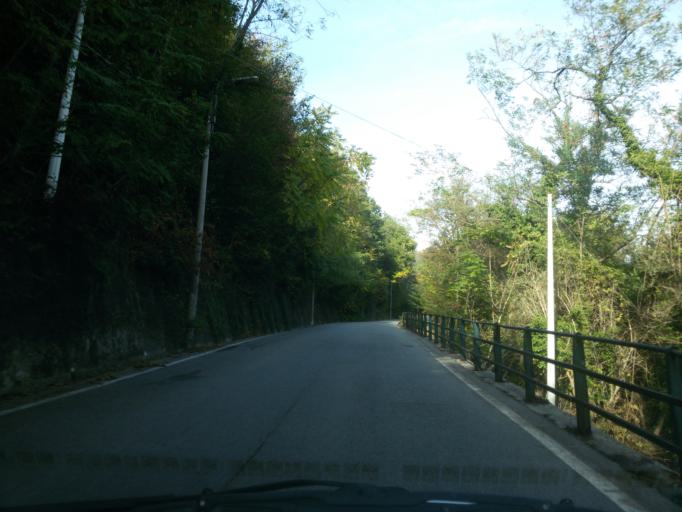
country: IT
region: Liguria
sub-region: Provincia di Genova
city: Piccarello
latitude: 44.4627
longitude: 8.9670
